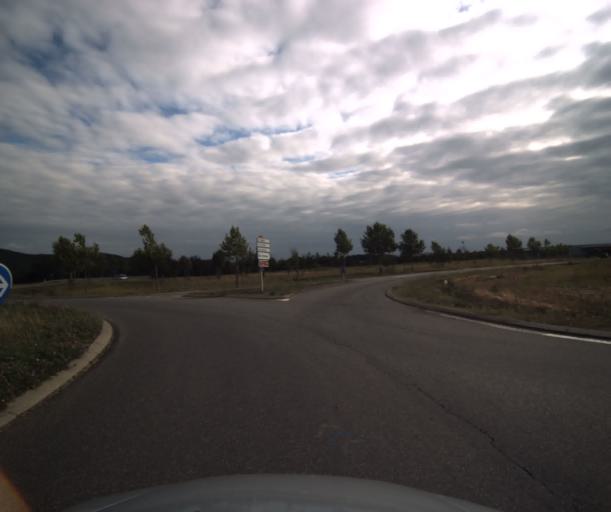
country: FR
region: Midi-Pyrenees
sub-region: Departement de la Haute-Garonne
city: Le Fauga
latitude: 43.4331
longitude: 1.3104
